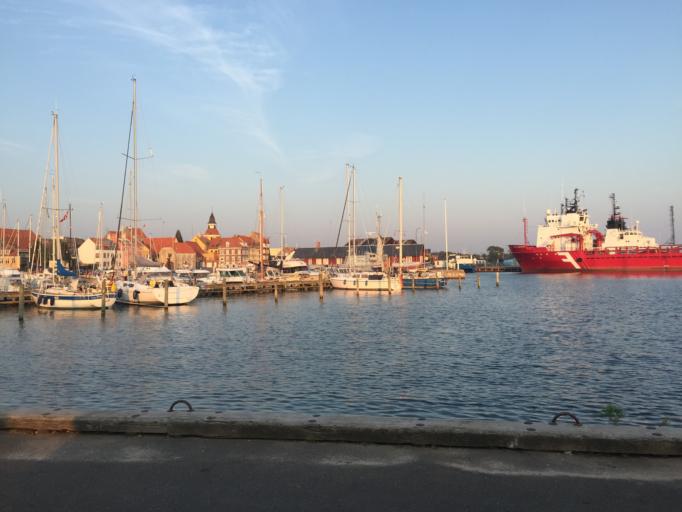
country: DK
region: South Denmark
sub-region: Faaborg-Midtfyn Kommune
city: Faaborg
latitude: 55.0943
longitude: 10.2374
